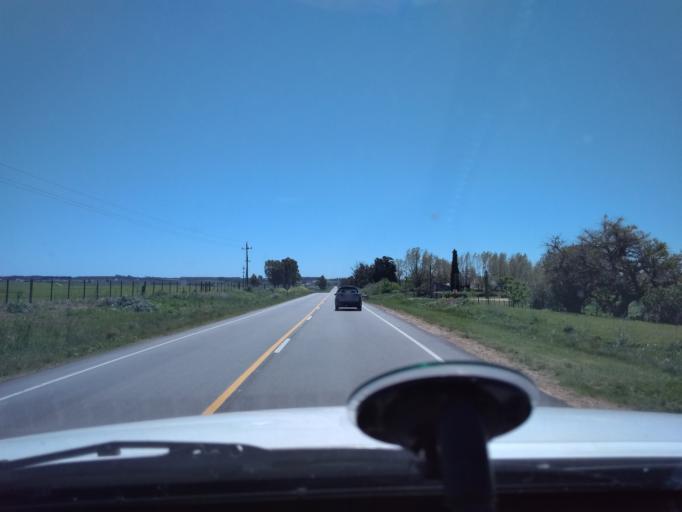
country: UY
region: Canelones
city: Las Piedras
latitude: -34.7095
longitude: -56.2909
